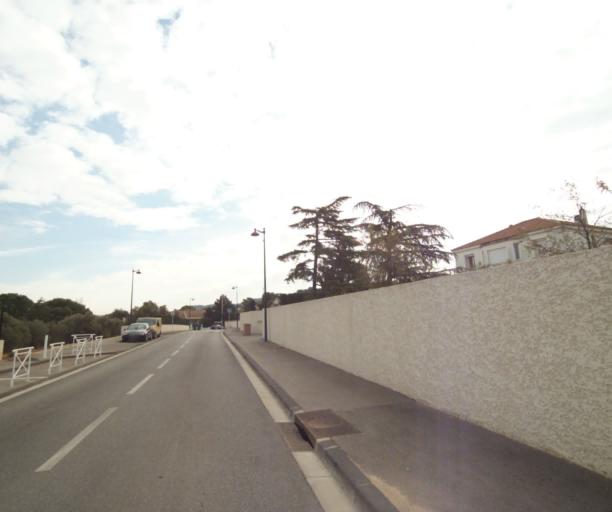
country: FR
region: Provence-Alpes-Cote d'Azur
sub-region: Departement des Bouches-du-Rhone
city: Saint-Victoret
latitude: 43.4114
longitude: 5.2574
